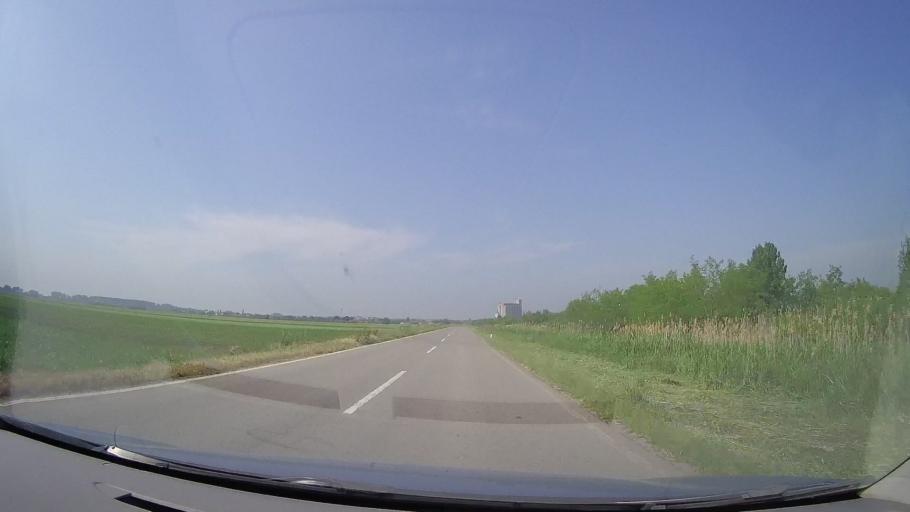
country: RS
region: Autonomna Pokrajina Vojvodina
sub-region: Srednjebanatski Okrug
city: Secanj
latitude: 45.3794
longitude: 20.7856
